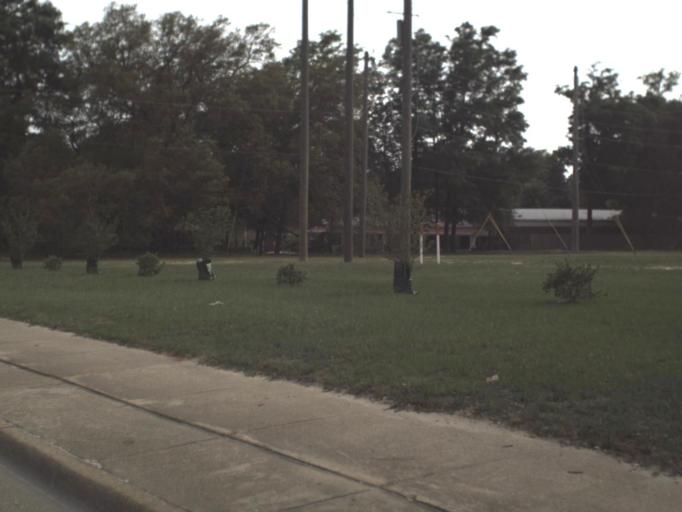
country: US
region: Florida
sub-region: Santa Rosa County
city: Milton
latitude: 30.6405
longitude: -87.0431
